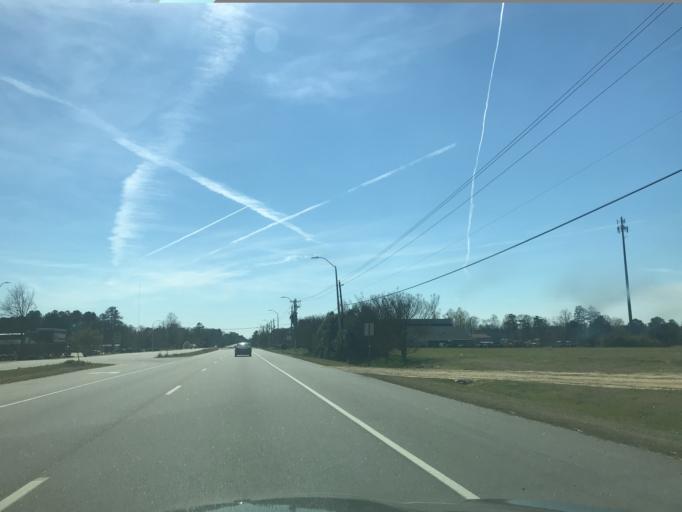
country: US
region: North Carolina
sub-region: Wake County
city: Fuquay-Varina
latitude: 35.6075
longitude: -78.7455
